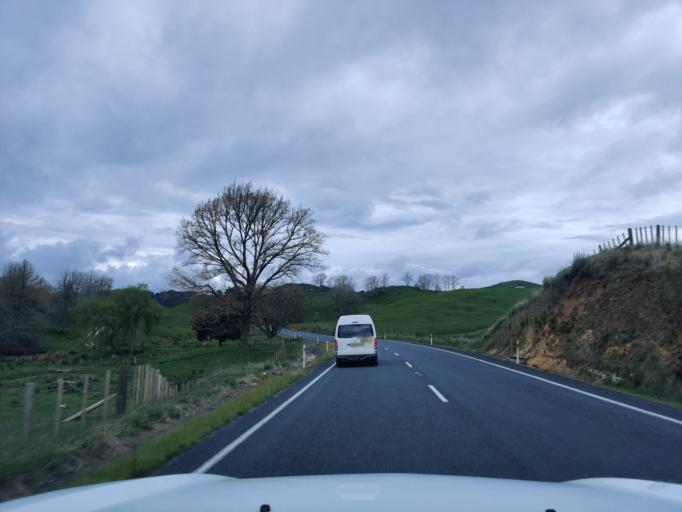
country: NZ
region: Waikato
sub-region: Otorohanga District
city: Otorohanga
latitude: -38.4527
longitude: 175.1637
